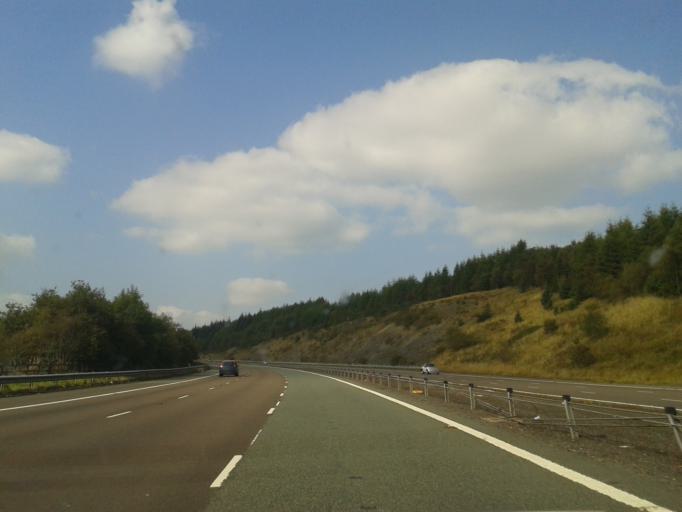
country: GB
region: Scotland
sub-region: Dumfries and Galloway
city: Moffat
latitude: 55.4079
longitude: -3.5611
